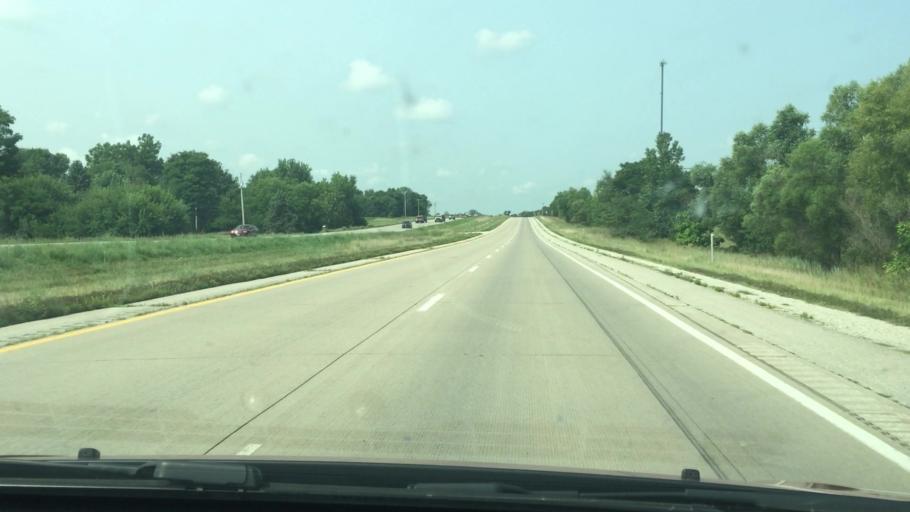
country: US
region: Iowa
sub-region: Cedar County
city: Durant
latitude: 41.5184
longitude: -90.8931
